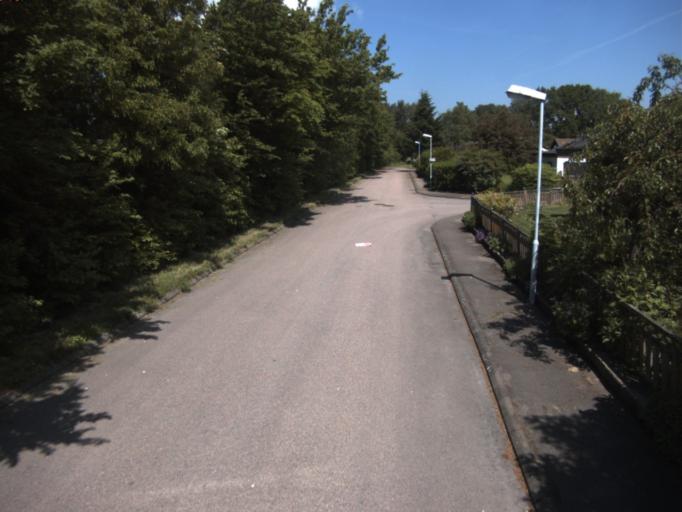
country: SE
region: Skane
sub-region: Helsingborg
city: Barslov
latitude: 56.0340
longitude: 12.8092
